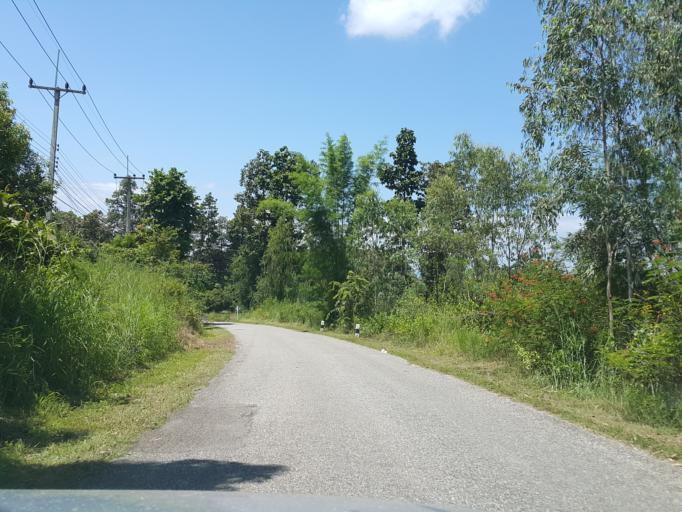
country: TH
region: Chiang Mai
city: San Kamphaeng
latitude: 18.7108
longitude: 99.1810
